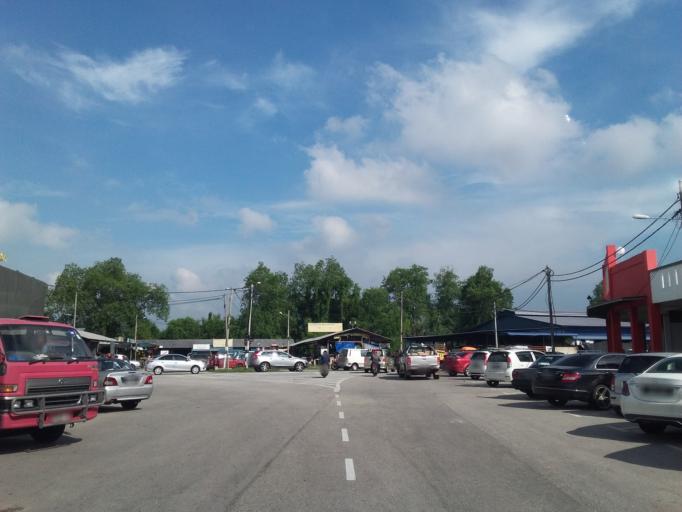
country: MY
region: Johor
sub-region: Daerah Batu Pahat
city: Batu Pahat
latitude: 1.8474
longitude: 102.9252
